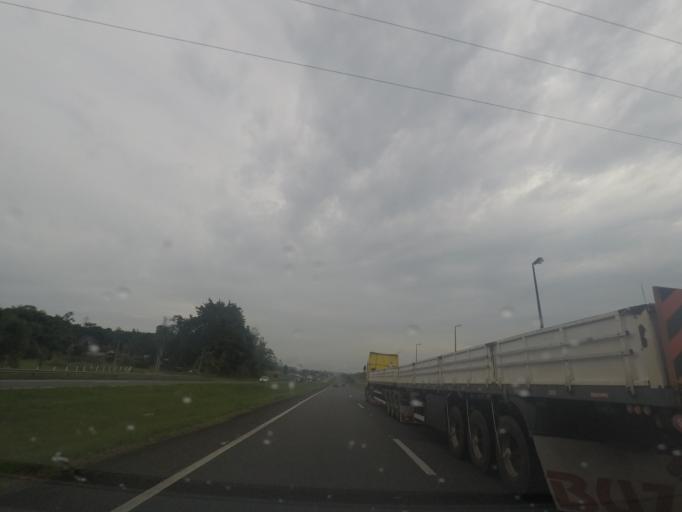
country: BR
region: Sao Paulo
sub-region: Pariquera-Acu
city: Pariquera Acu
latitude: -24.6257
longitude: -47.8993
